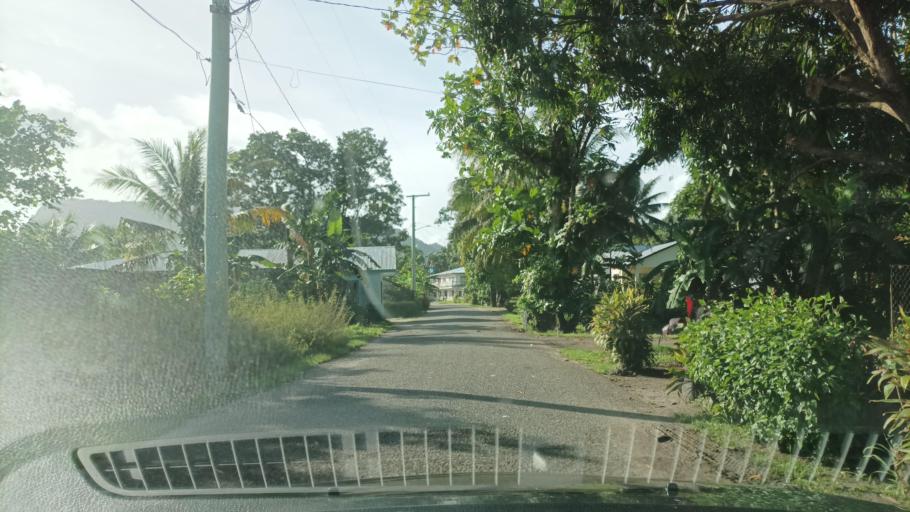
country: FM
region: Kosrae
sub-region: Lelu Municipality
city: Lelu
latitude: 5.3291
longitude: 163.0263
